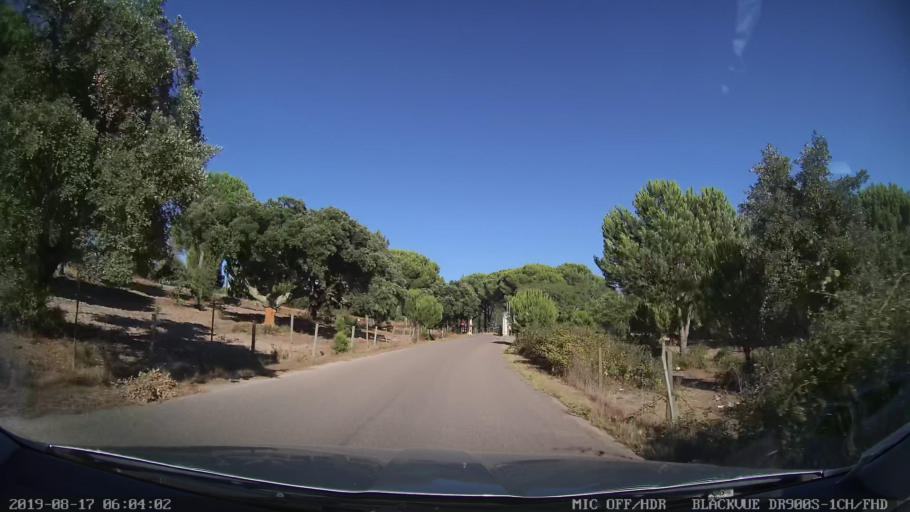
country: PT
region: Santarem
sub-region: Benavente
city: Poceirao
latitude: 38.8464
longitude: -8.7084
